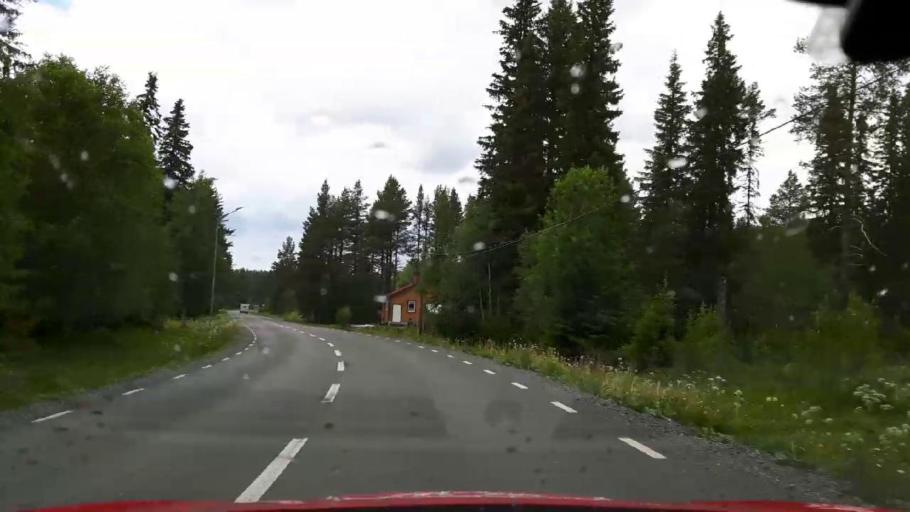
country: SE
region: Jaemtland
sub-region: Krokoms Kommun
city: Krokom
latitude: 63.5632
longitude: 14.2764
